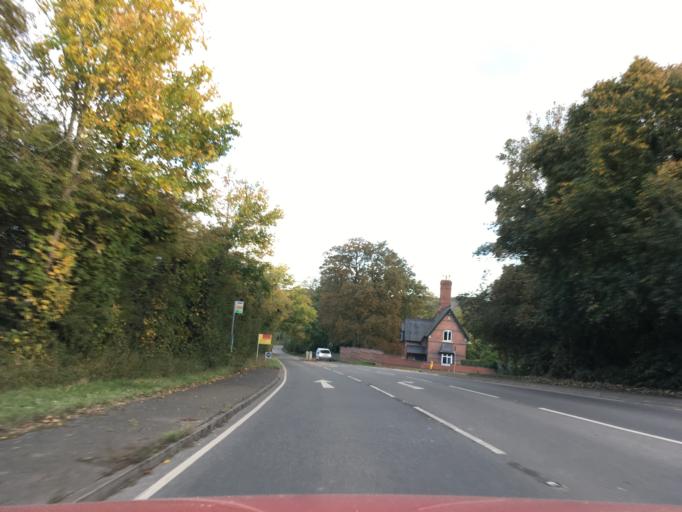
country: GB
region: England
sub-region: Herefordshire
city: Withington
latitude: 52.0635
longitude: -2.6298
